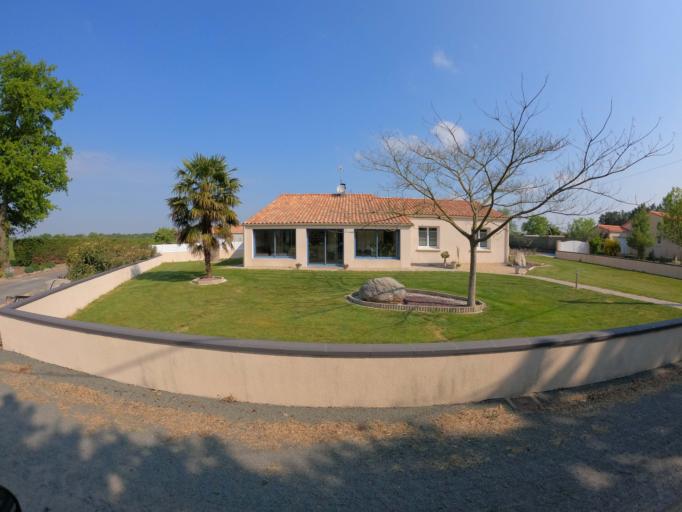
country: FR
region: Pays de la Loire
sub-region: Departement de la Vendee
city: La Bruffiere
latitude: 47.0086
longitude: -1.2082
